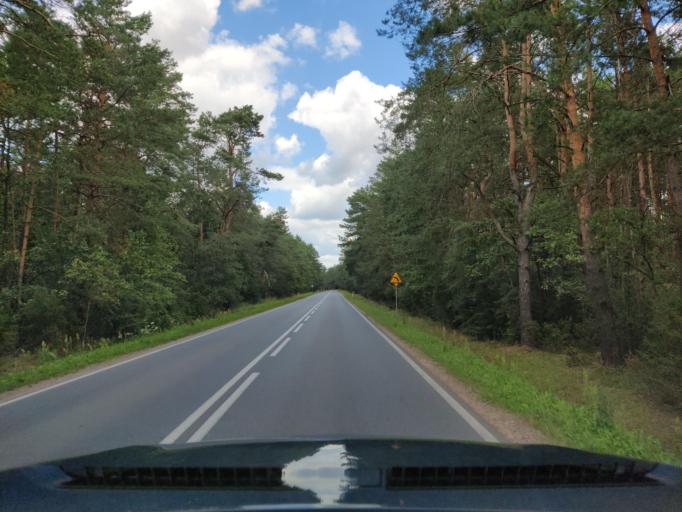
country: PL
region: Masovian Voivodeship
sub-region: Powiat wegrowski
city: Liw
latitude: 52.3488
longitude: 21.9521
